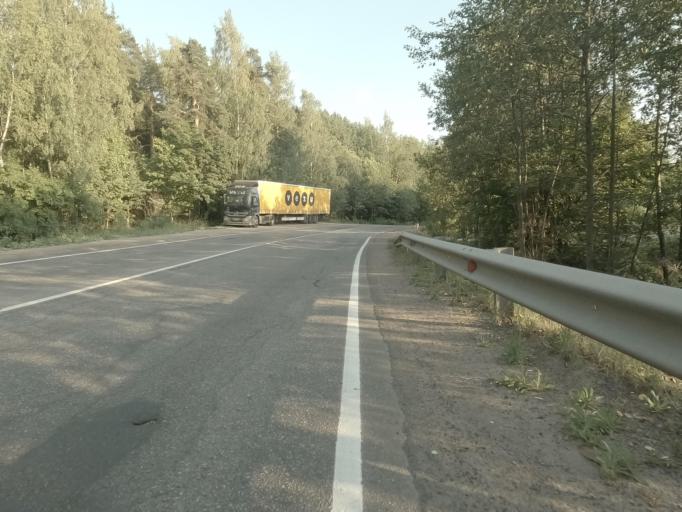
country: RU
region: Leningrad
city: Vyborg
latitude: 60.7294
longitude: 28.7599
